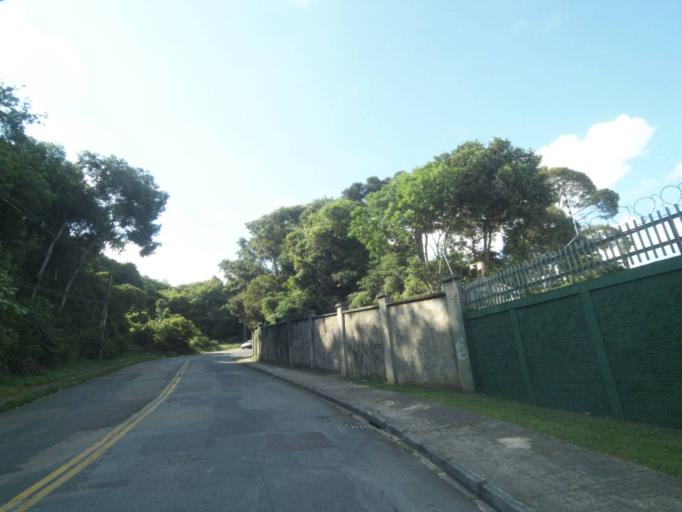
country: BR
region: Parana
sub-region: Curitiba
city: Curitiba
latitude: -25.3855
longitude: -49.3038
